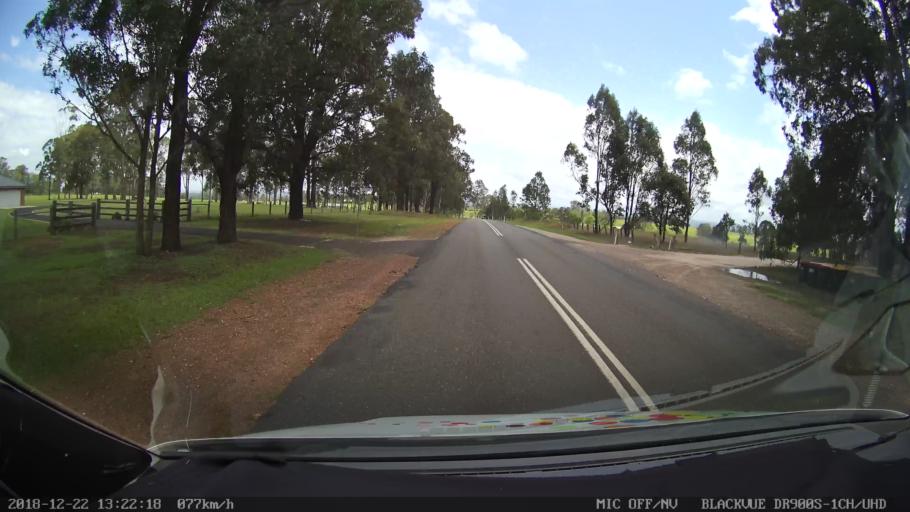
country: AU
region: New South Wales
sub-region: Clarence Valley
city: Coutts Crossing
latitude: -29.7852
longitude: 152.9126
